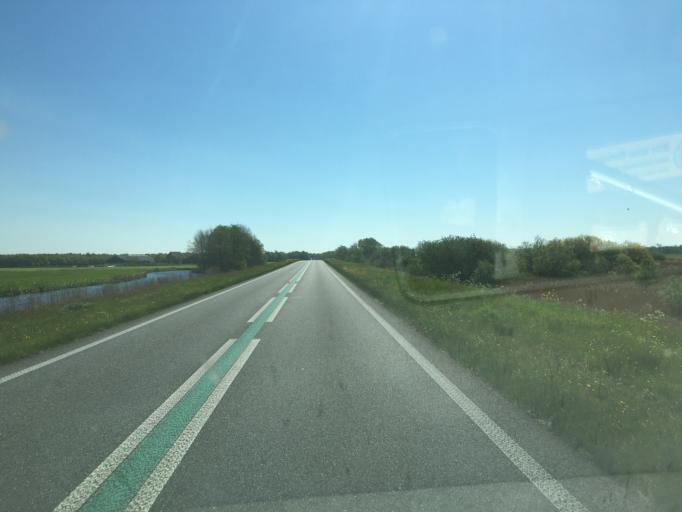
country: NL
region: Friesland
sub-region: Gemeente Gaasterlan-Sleat
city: Oudemirdum
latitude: 52.8811
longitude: 5.4984
